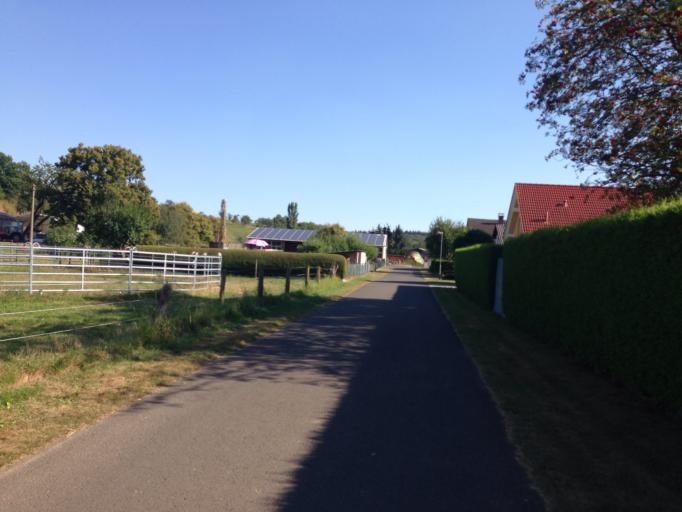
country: DE
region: Hesse
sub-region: Regierungsbezirk Giessen
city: Rabenau
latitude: 50.6484
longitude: 8.8958
